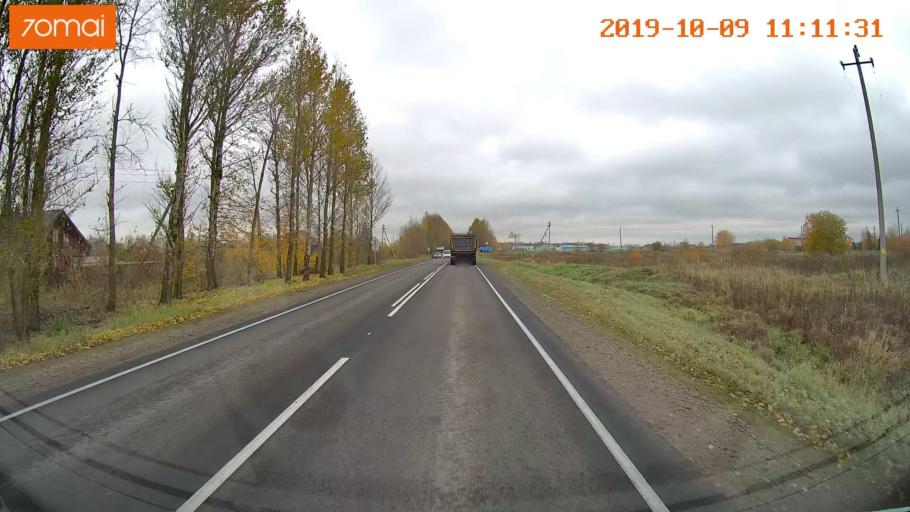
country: RU
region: Vologda
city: Vologda
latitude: 59.1687
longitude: 39.8213
